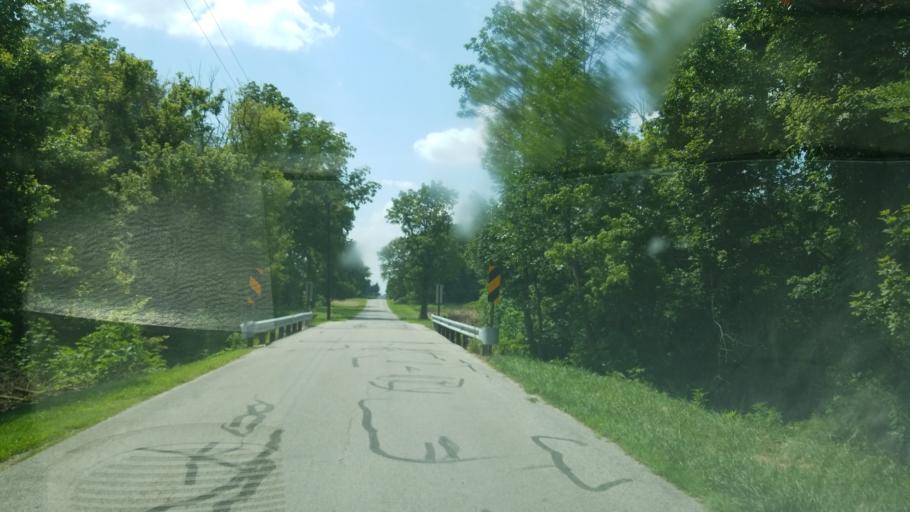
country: US
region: Ohio
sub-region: Seneca County
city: Tiffin
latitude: 41.1528
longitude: -83.2061
